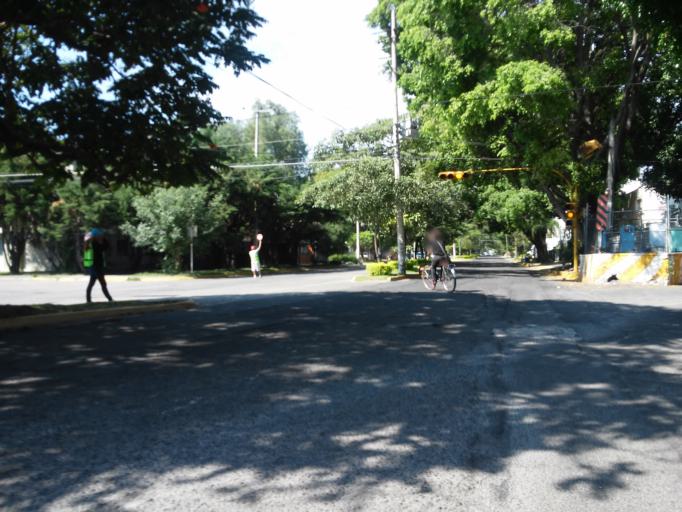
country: MX
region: Jalisco
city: Guadalajara
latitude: 20.6579
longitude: -103.3933
